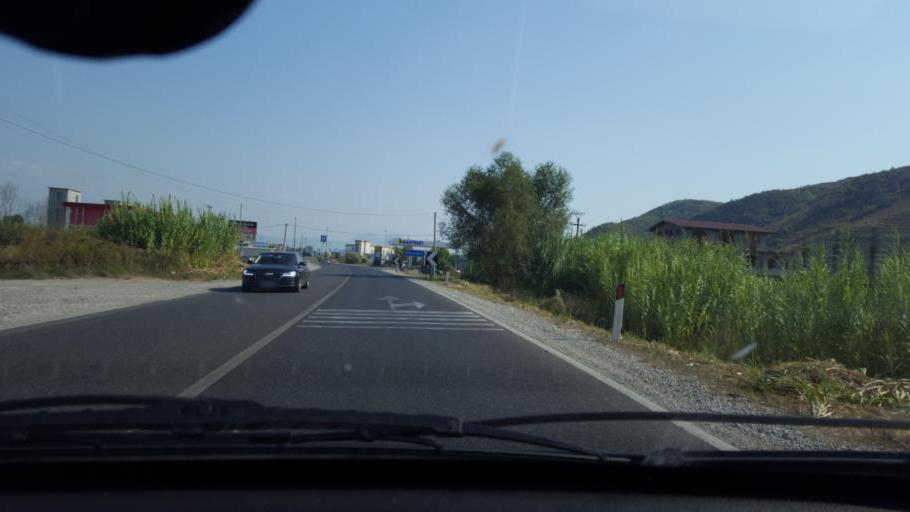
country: AL
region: Shkoder
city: Vukatane
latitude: 41.9967
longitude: 19.5278
